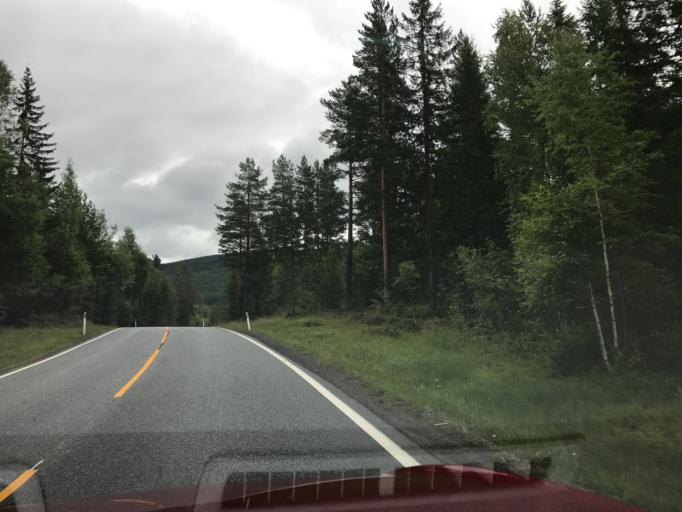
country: NO
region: Buskerud
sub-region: Rollag
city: Rollag
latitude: 60.0127
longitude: 9.2608
